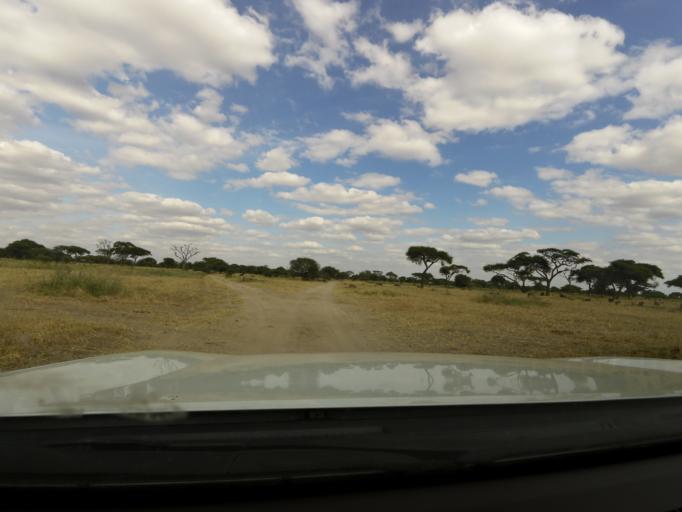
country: TZ
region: Manyara
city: Magugu
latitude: -3.7708
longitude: 35.9703
